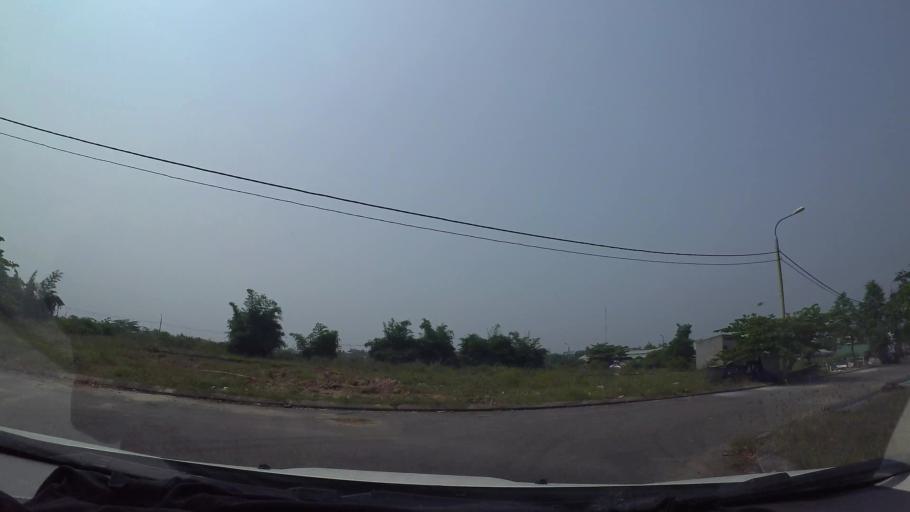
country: VN
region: Da Nang
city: Cam Le
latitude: 15.9806
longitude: 108.2104
